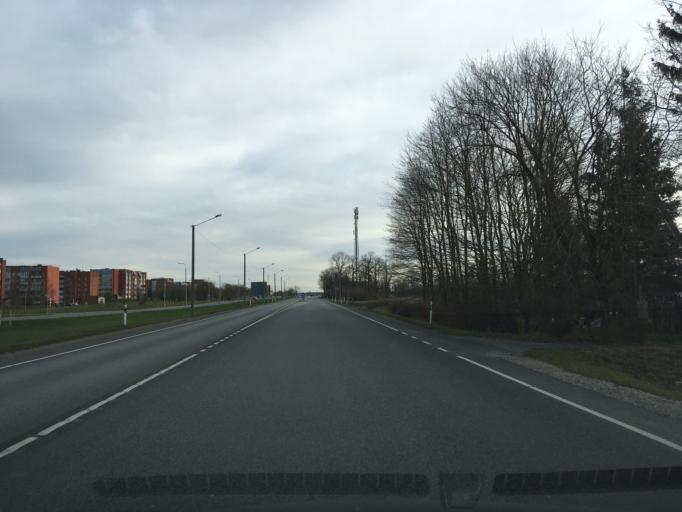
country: EE
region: Ida-Virumaa
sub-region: Sillamaee linn
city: Sillamae
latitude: 59.3901
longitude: 27.7817
